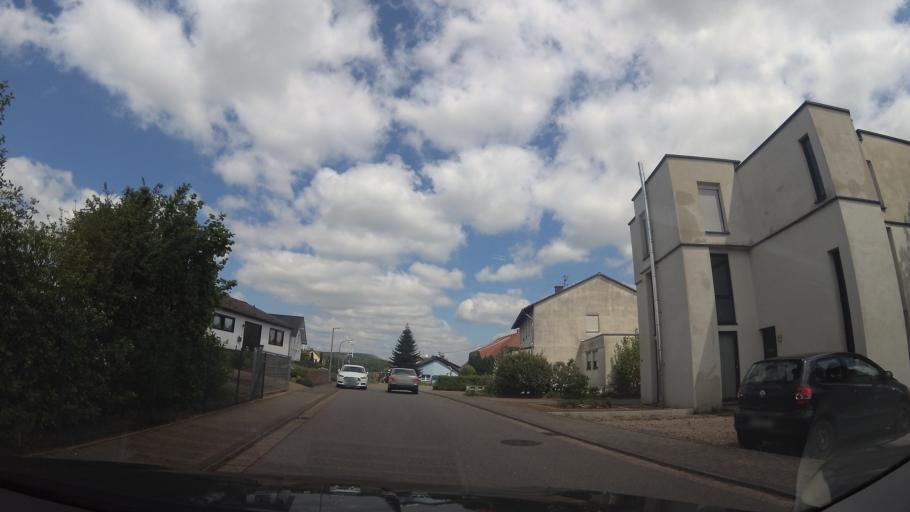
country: DE
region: Saarland
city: Lebach
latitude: 49.4192
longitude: 6.9184
